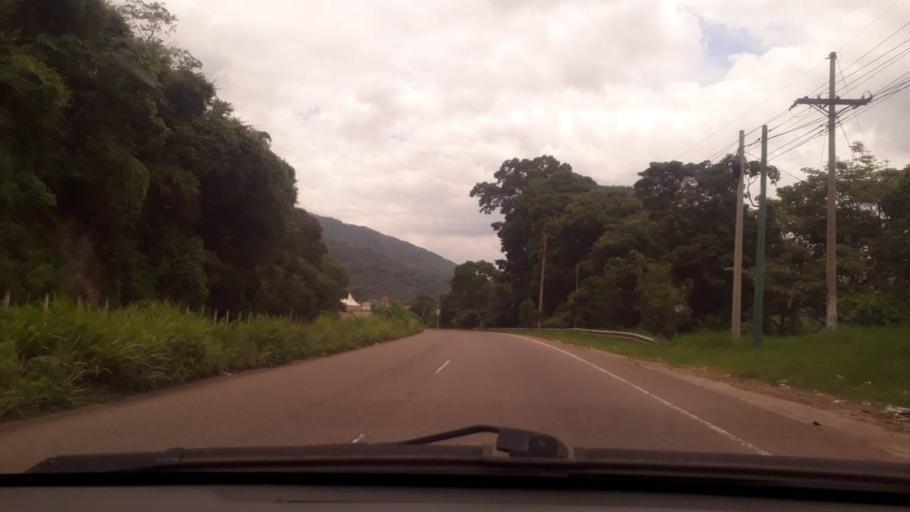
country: GT
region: Santa Rosa
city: Oratorio
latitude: 14.2563
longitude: -90.2206
